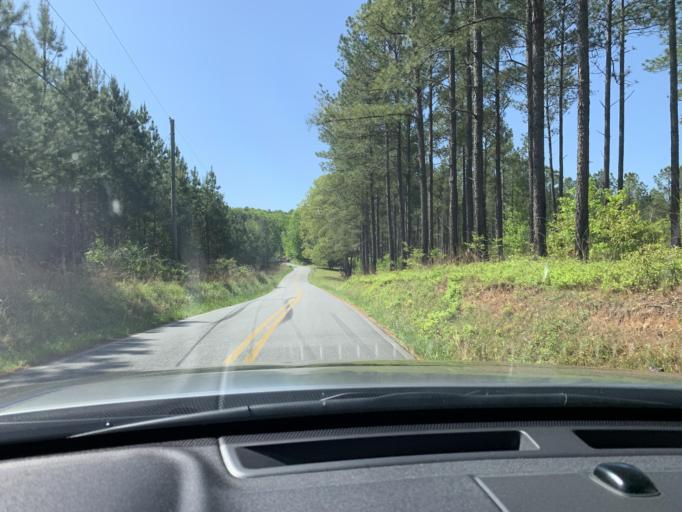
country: US
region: Georgia
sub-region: Haralson County
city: Buchanan
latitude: 33.9154
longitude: -85.2026
